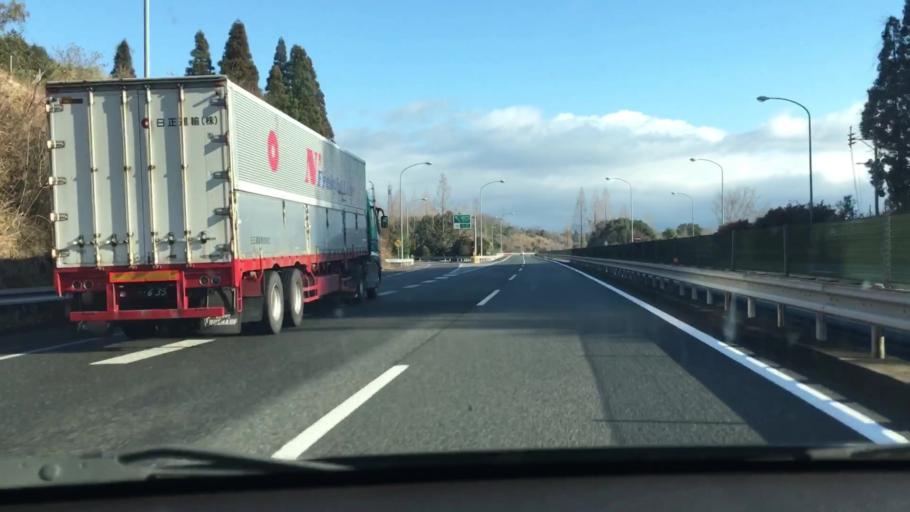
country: JP
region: Kumamoto
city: Hitoyoshi
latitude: 32.2335
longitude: 130.7678
